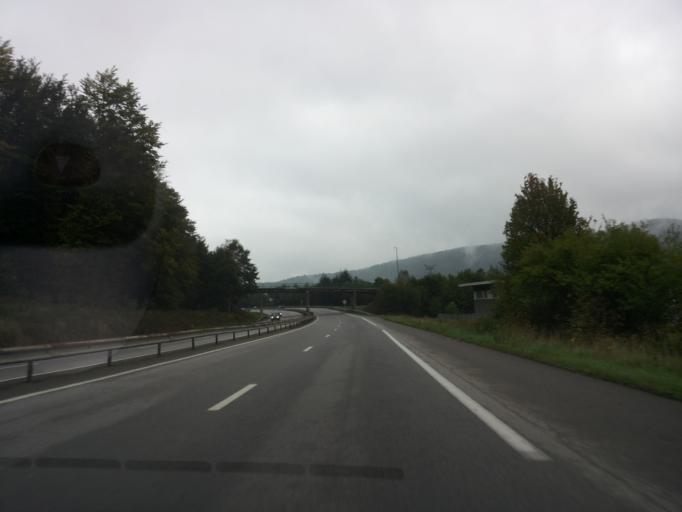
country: FR
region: Lorraine
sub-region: Departement des Vosges
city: Eloyes
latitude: 48.0857
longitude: 6.5971
